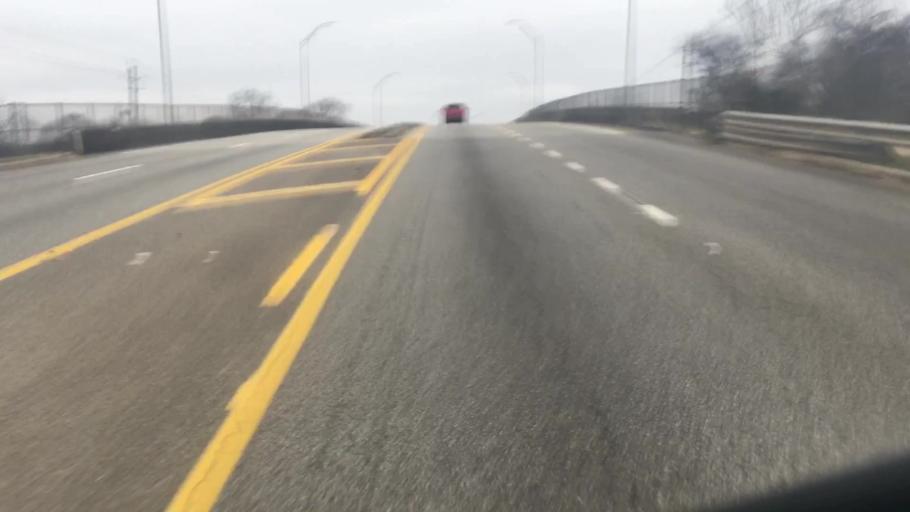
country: US
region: Alabama
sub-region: Jefferson County
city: Birmingham
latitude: 33.5428
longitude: -86.8139
